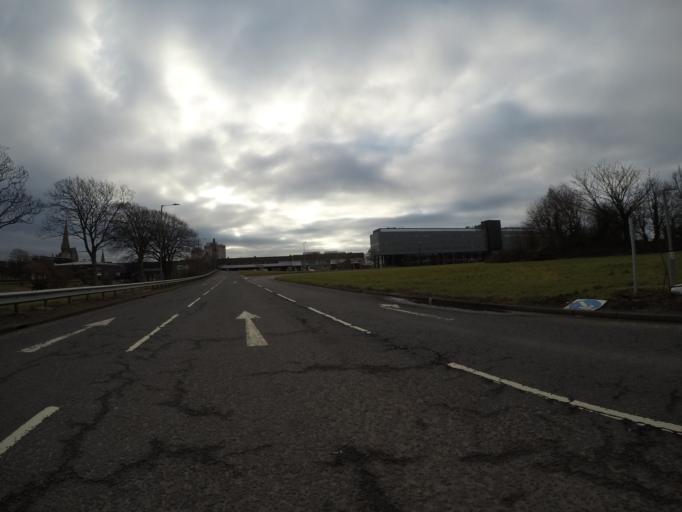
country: GB
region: Scotland
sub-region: North Ayrshire
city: Irvine
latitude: 55.6147
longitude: -4.6738
